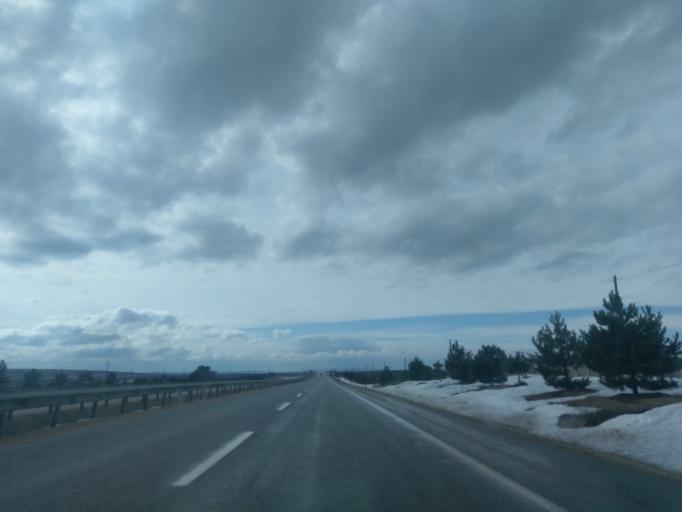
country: TR
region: Eskisehir
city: Inonu
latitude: 39.7232
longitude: 30.2589
